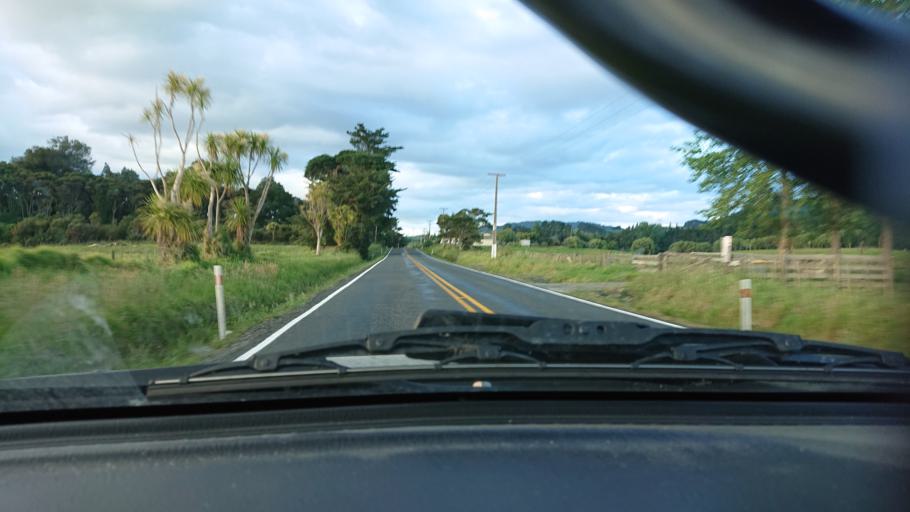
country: NZ
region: Auckland
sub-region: Auckland
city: Parakai
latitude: -36.4940
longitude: 174.4484
